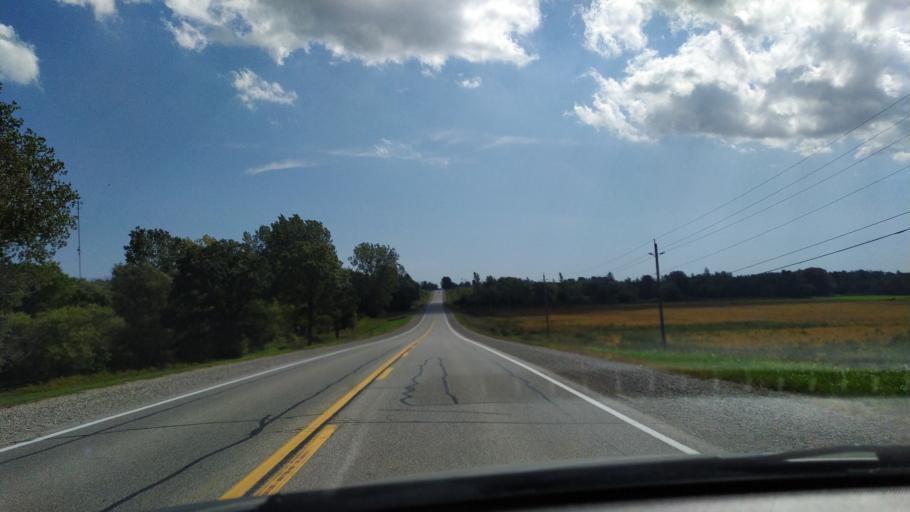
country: CA
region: Ontario
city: Ingersoll
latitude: 43.1421
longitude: -80.8944
